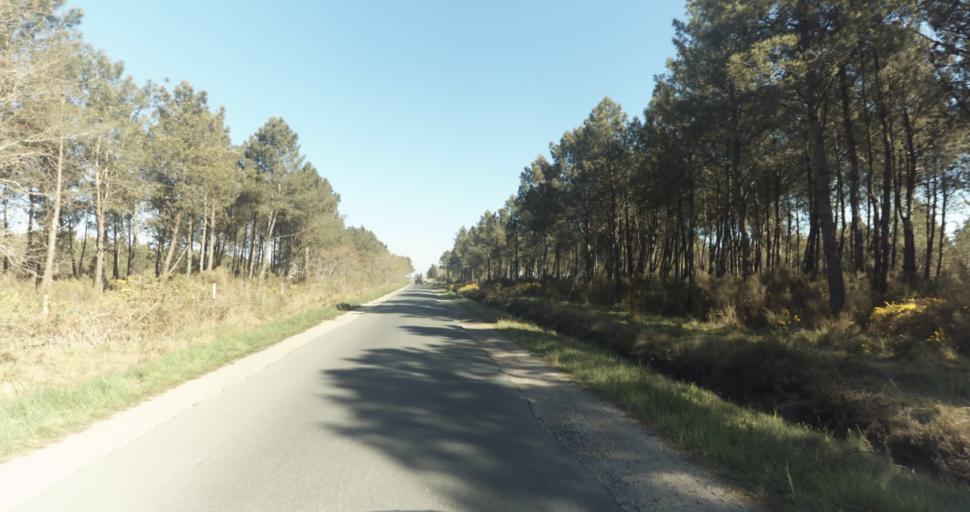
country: FR
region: Aquitaine
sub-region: Departement de la Gironde
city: Marcheprime
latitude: 44.7606
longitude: -0.8525
